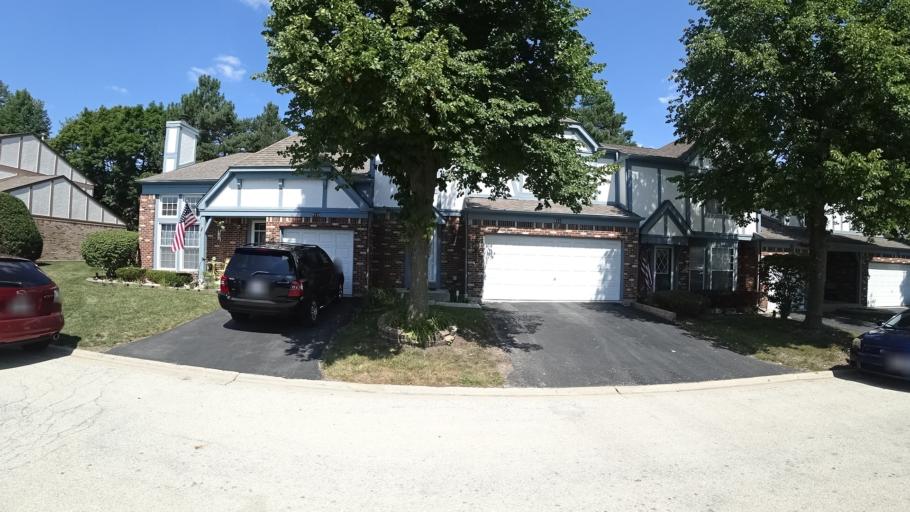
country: US
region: Illinois
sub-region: Cook County
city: Orland Park
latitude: 41.6227
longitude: -87.8401
